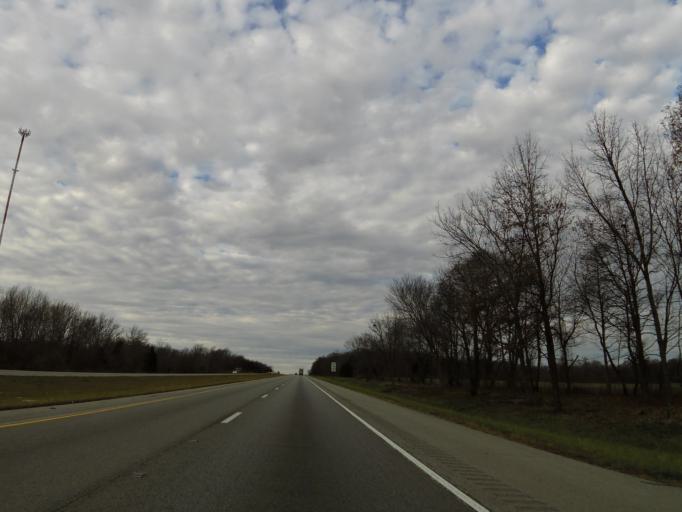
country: US
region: Illinois
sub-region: Jefferson County
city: Mount Vernon
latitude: 38.3623
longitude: -89.0433
